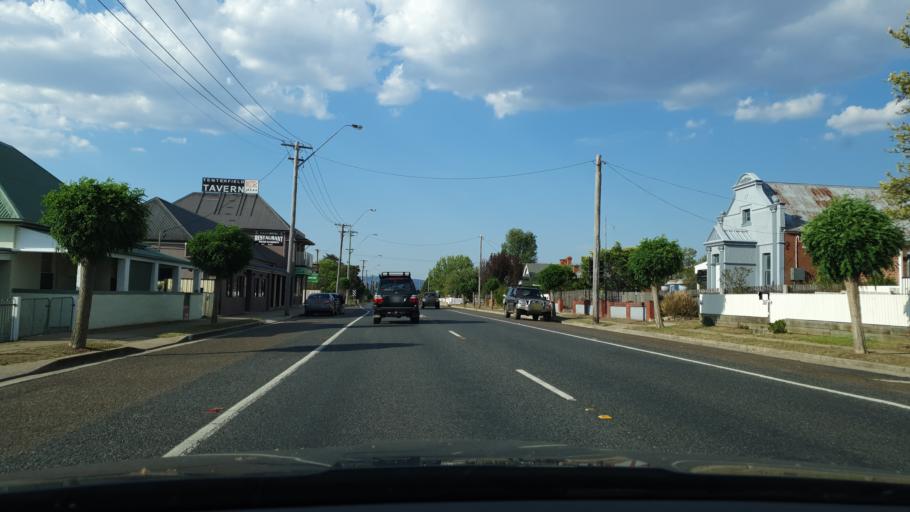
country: AU
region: New South Wales
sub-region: Tenterfield Municipality
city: Carrolls Creek
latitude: -29.0506
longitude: 152.0197
